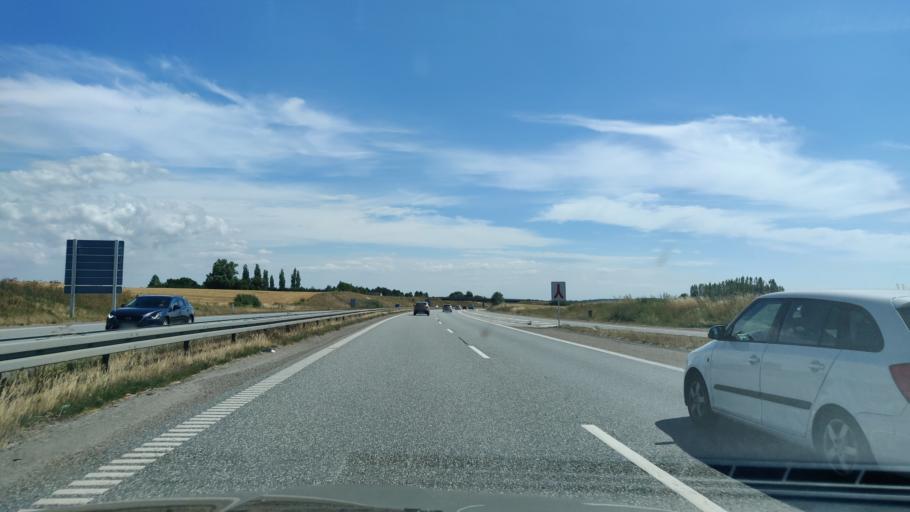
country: DK
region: Zealand
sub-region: Holbaek Kommune
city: Holbaek
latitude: 55.7001
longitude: 11.6580
